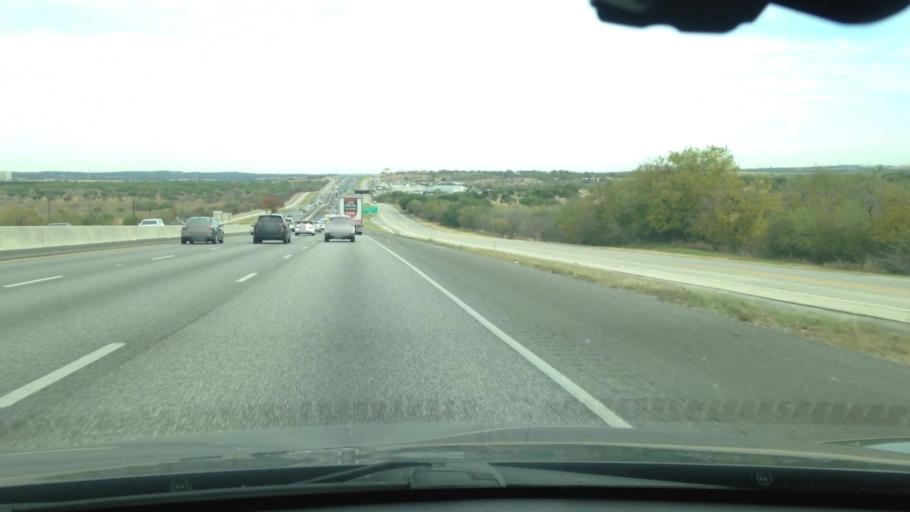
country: US
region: Texas
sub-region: Guadalupe County
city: Lake Dunlap
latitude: 29.7603
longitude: -98.0481
